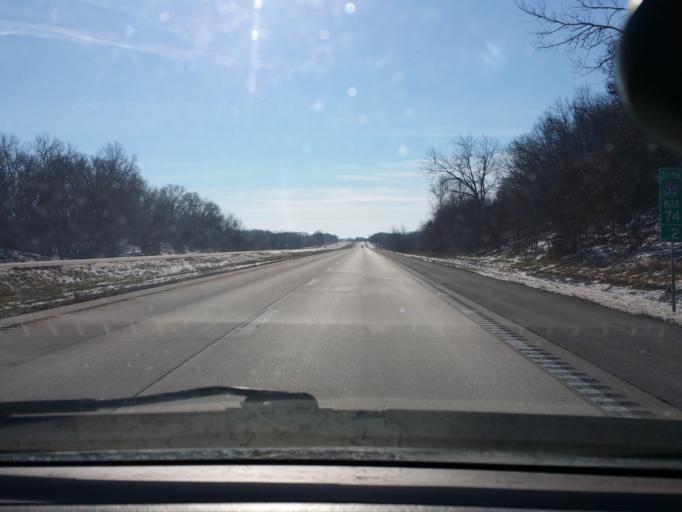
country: US
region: Missouri
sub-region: Daviess County
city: Gallatin
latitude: 40.0214
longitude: -94.0961
